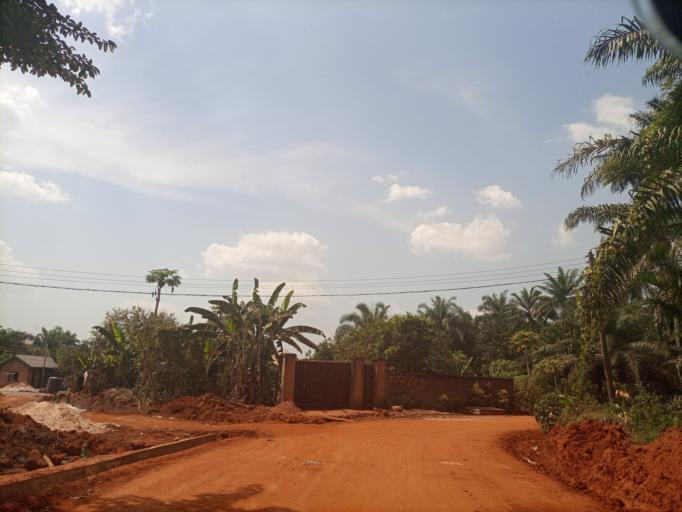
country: NG
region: Enugu
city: Obollo-Afor
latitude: 6.8670
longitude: 7.4726
